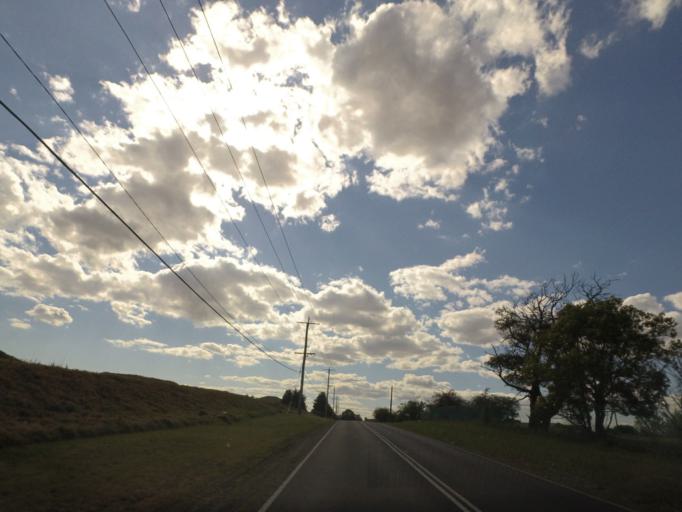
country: AU
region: Victoria
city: Heatherton
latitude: -37.9693
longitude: 145.1157
